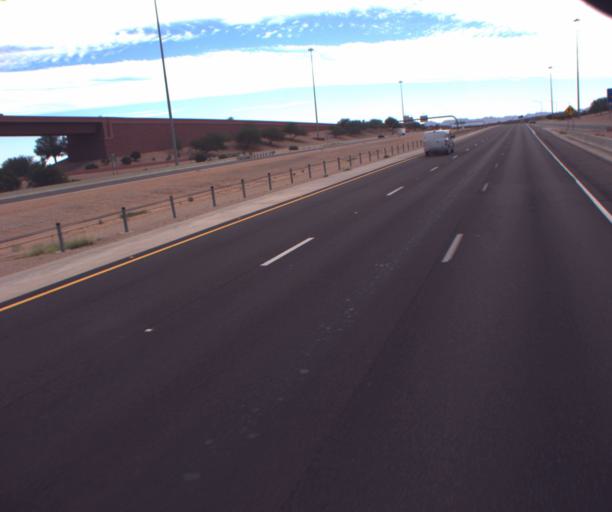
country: US
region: Arizona
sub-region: Pinal County
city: Apache Junction
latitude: 33.3843
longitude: -111.6485
